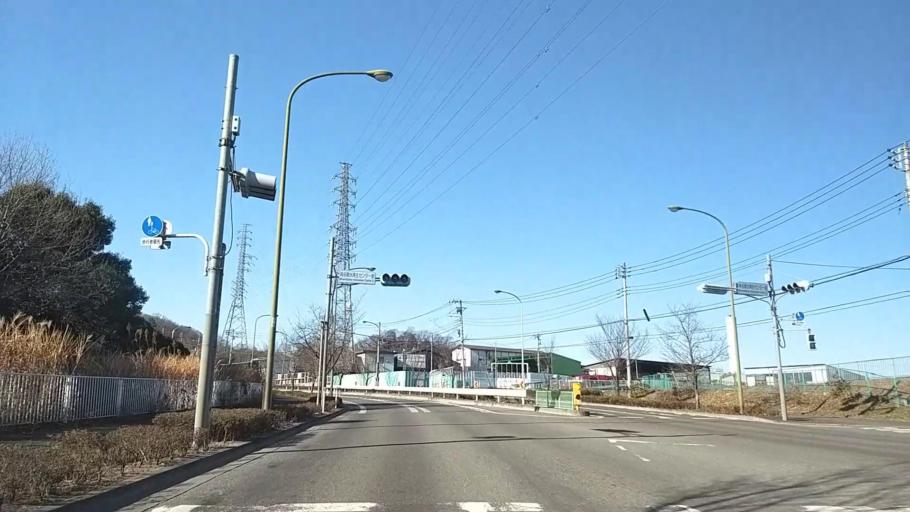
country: JP
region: Tokyo
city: Kokubunji
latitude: 35.6470
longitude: 139.4808
